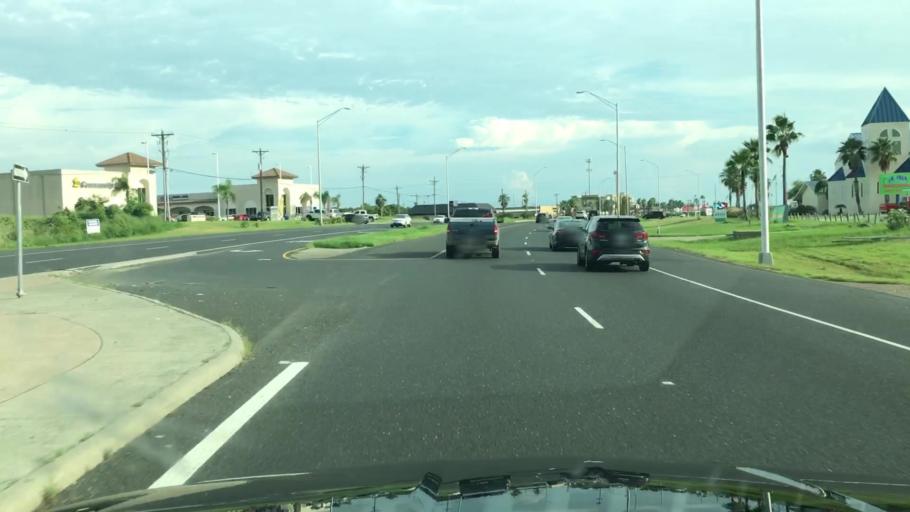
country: US
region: Texas
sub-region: Nueces County
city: Corpus Christi
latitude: 27.6255
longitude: -97.2222
